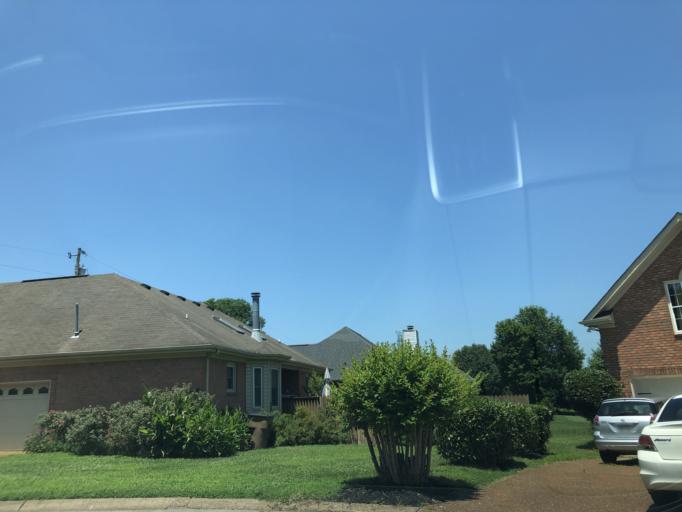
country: US
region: Tennessee
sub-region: Williamson County
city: Nolensville
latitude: 36.0368
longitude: -86.6745
